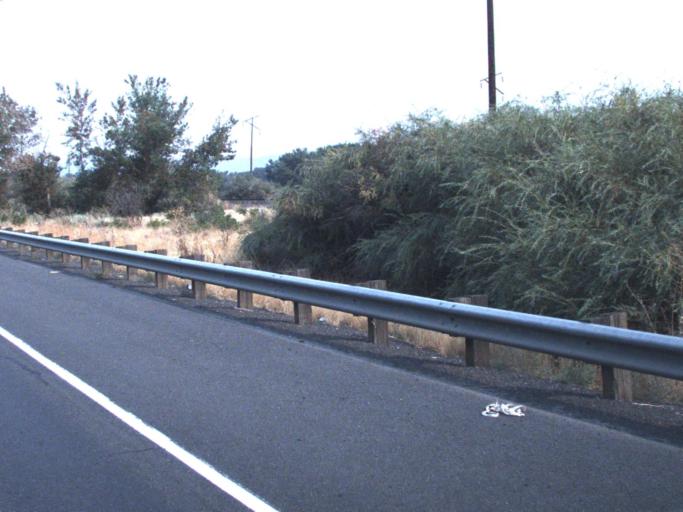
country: US
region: Washington
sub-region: Yakima County
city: Wapato
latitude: 46.4695
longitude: -120.4404
